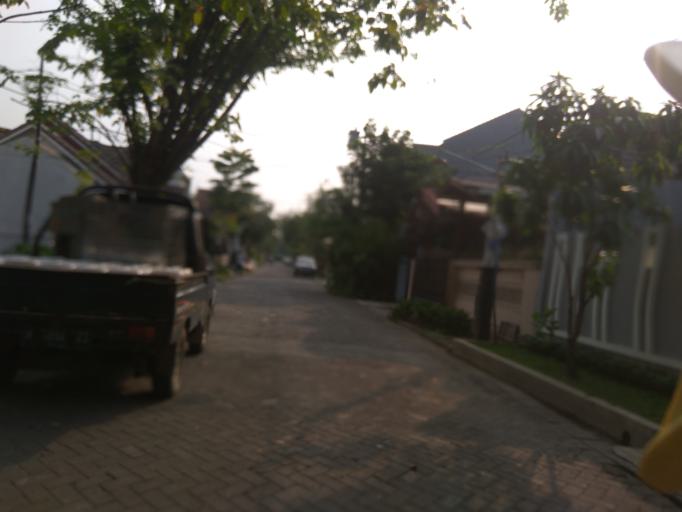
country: ID
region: Central Java
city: Semarang
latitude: -6.9696
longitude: 110.3989
